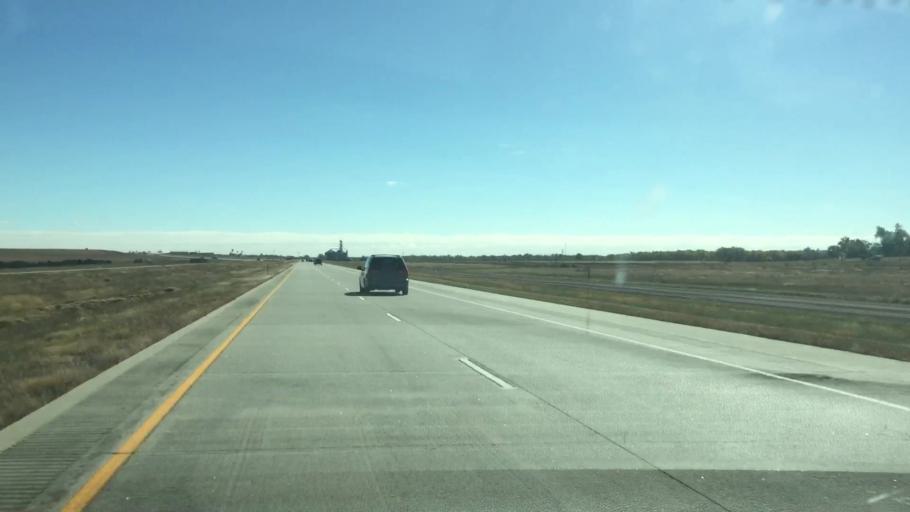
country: US
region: Colorado
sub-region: Lincoln County
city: Limon
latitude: 39.2759
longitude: -103.7478
